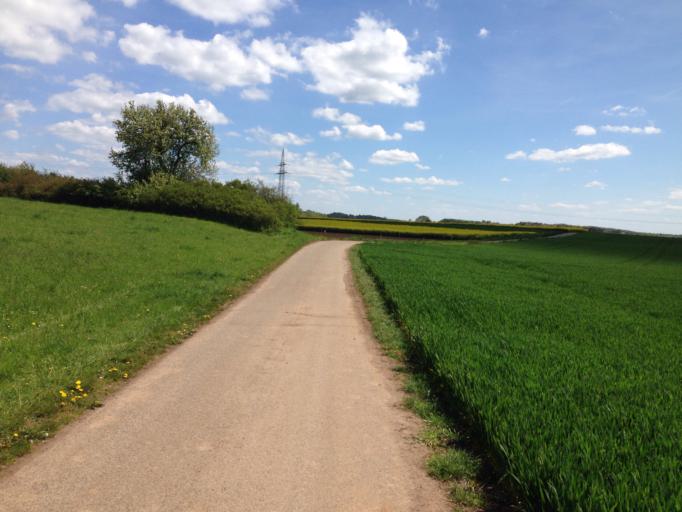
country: DE
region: Hesse
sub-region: Regierungsbezirk Giessen
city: Lich
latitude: 50.5113
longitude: 8.8428
